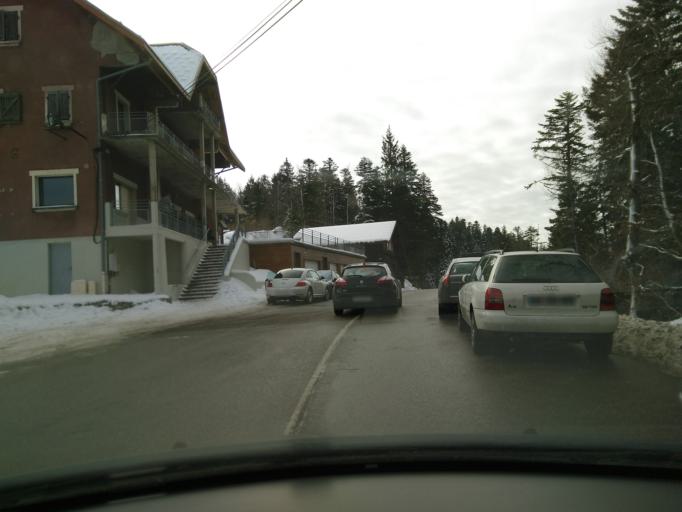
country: FR
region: Rhone-Alpes
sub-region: Departement de l'Isere
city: Le Sappey-en-Chartreuse
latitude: 45.2899
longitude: 5.7670
